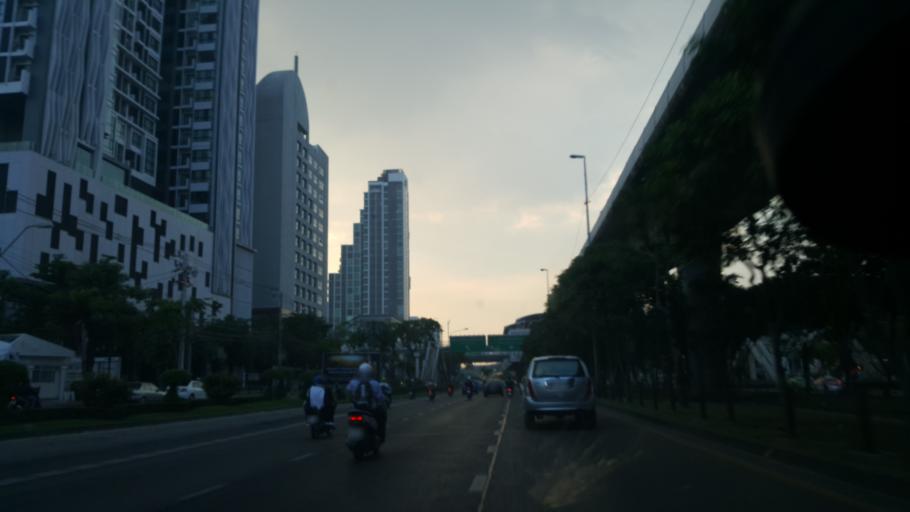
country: TH
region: Bangkok
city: Thon Buri
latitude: 13.7209
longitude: 100.4979
